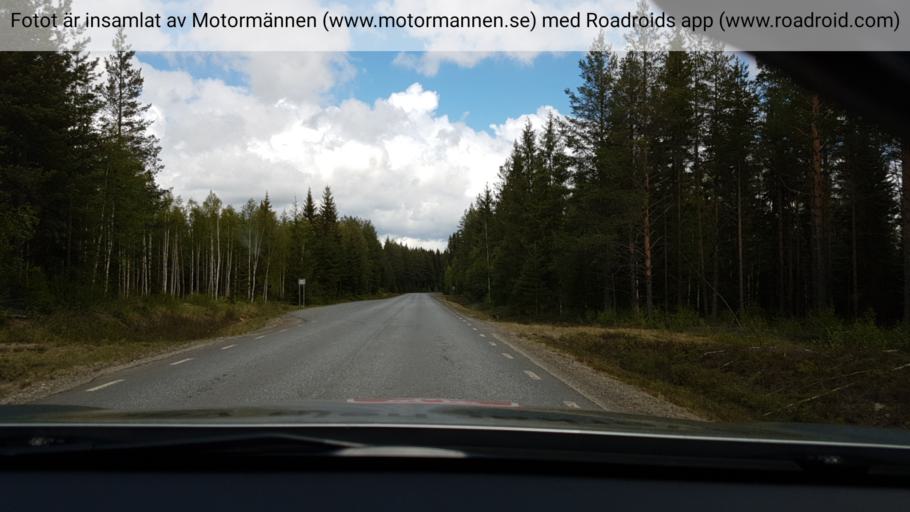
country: SE
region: Vaesterbotten
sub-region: Vindelns Kommun
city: Vindeln
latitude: 64.1814
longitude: 19.6770
